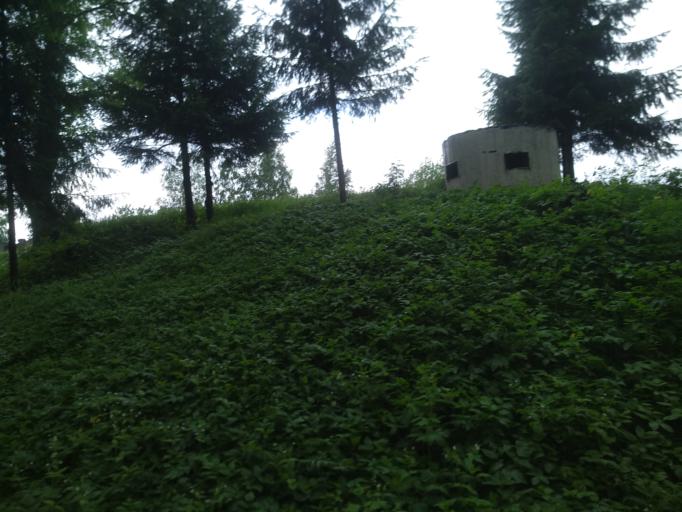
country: RU
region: Leningrad
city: Sosnovyy Bor
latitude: 59.9901
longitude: 29.2115
